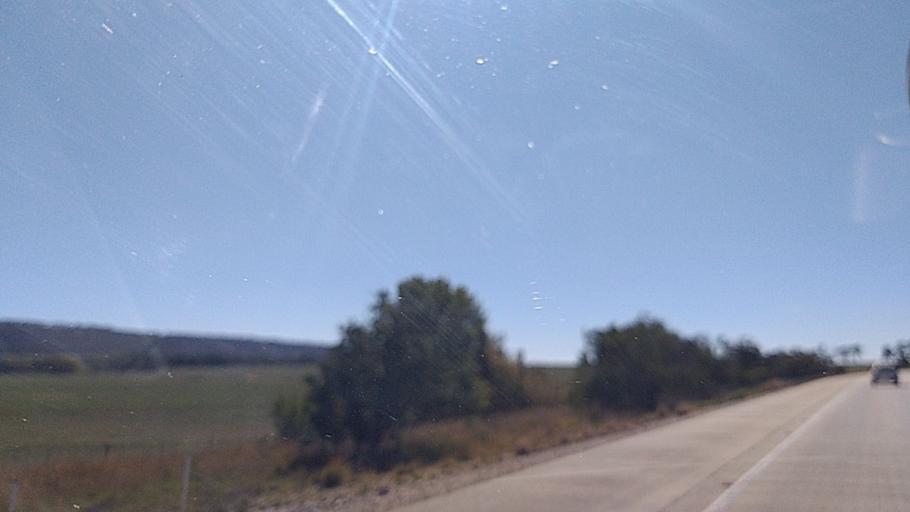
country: AU
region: New South Wales
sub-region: Yass Valley
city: Gundaroo
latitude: -34.9470
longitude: 149.4123
